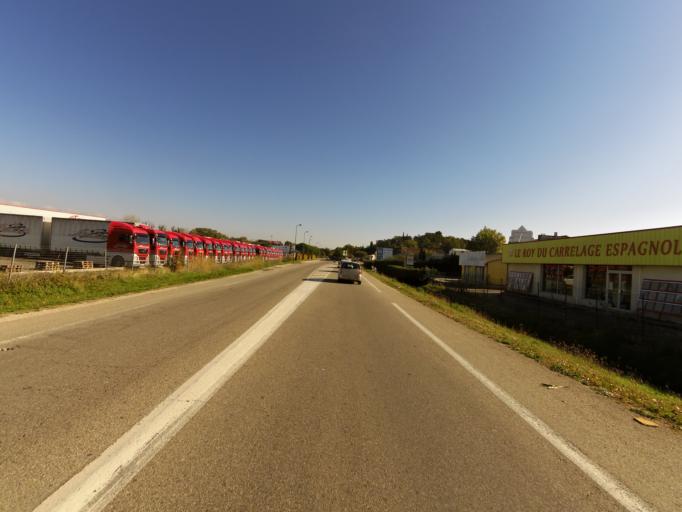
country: FR
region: Provence-Alpes-Cote d'Azur
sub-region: Departement du Vaucluse
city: Sarrians
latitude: 44.0816
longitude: 4.9799
